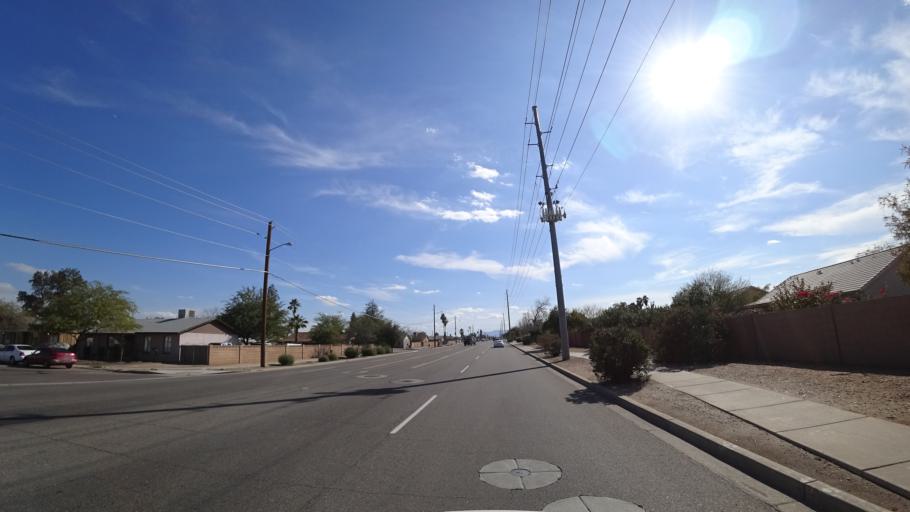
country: US
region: Arizona
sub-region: Maricopa County
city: Peoria
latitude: 33.5872
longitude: -112.2203
